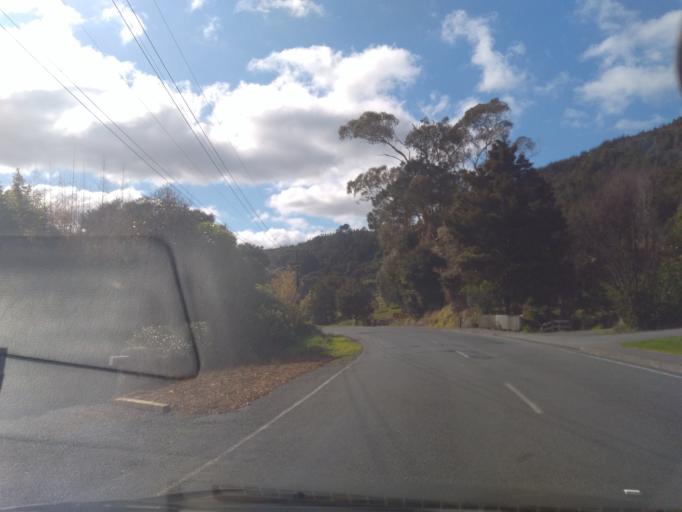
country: NZ
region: Northland
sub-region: Whangarei
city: Whangarei
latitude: -35.7002
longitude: 174.3345
